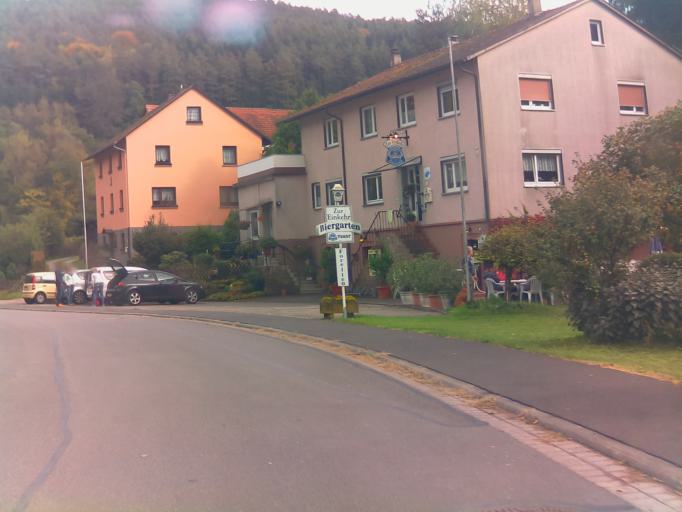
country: DE
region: Bavaria
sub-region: Regierungsbezirk Unterfranken
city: Kirchzell
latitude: 49.6283
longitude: 9.1369
